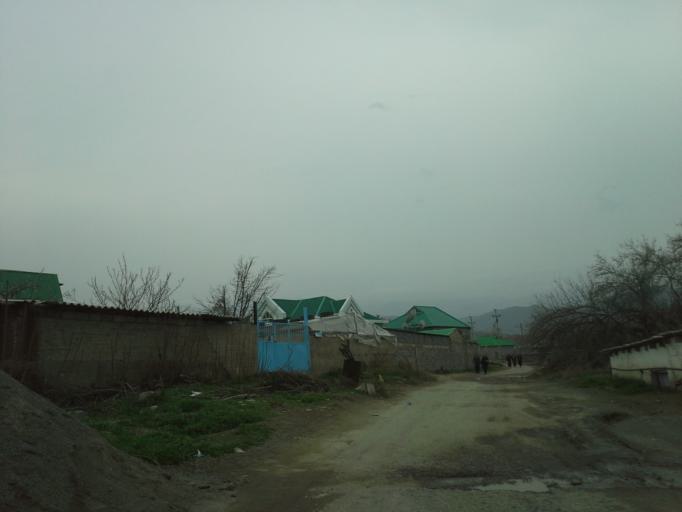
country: TM
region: Ahal
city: Abadan
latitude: 37.9682
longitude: 58.2210
